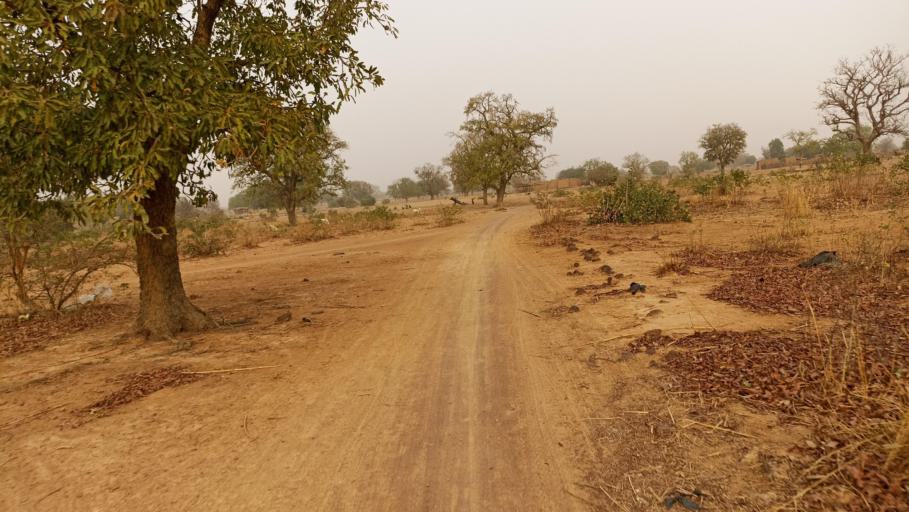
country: BF
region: Boucle du Mouhoun
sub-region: Province du Nayala
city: Toma
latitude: 12.8556
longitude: -2.7993
